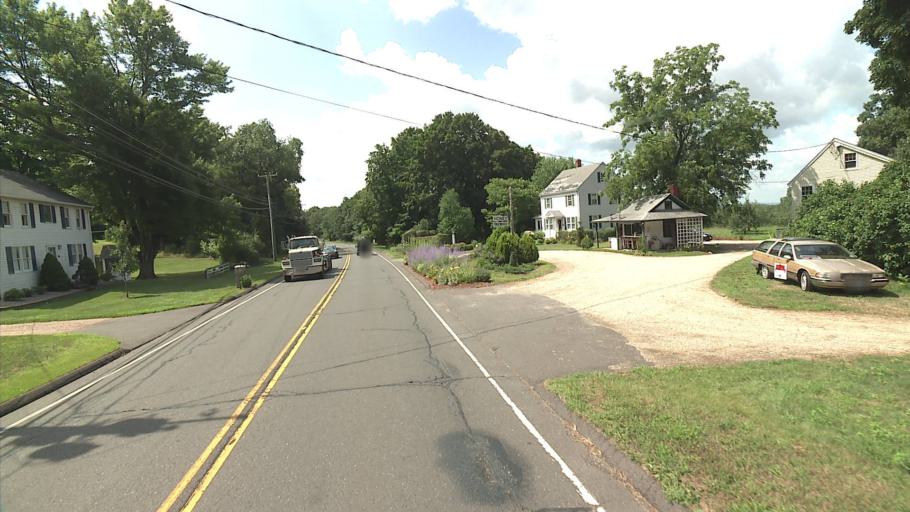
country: US
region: Connecticut
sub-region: Hartford County
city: Glastonbury Center
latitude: 41.6484
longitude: -72.6051
